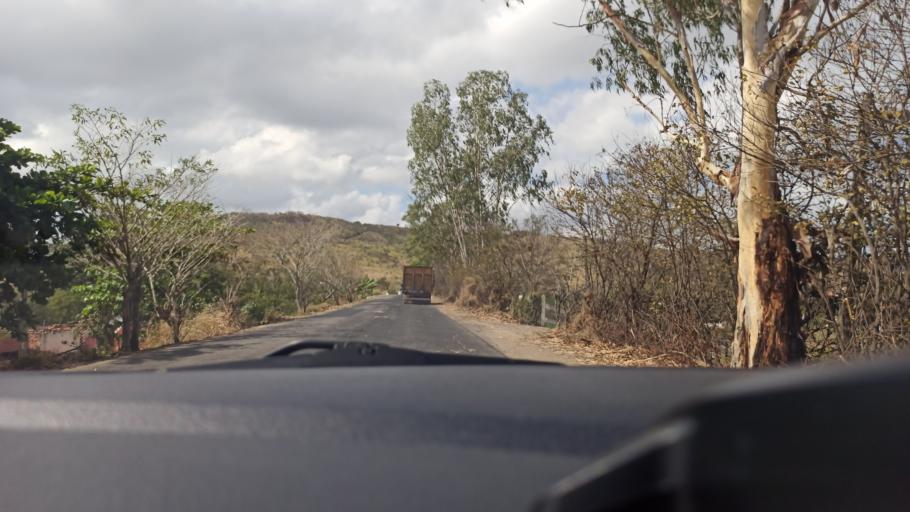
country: BR
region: Pernambuco
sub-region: Timbauba
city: Timbauba
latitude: -7.5160
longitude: -35.3040
